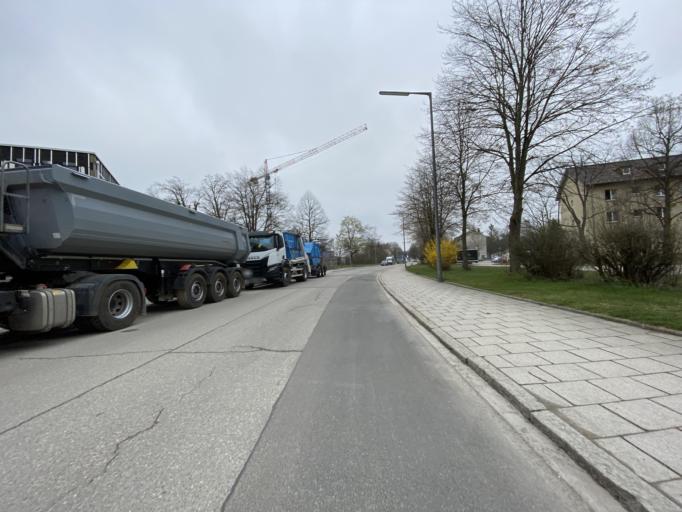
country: DE
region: Bavaria
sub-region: Upper Bavaria
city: Oberschleissheim
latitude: 48.2069
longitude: 11.5786
